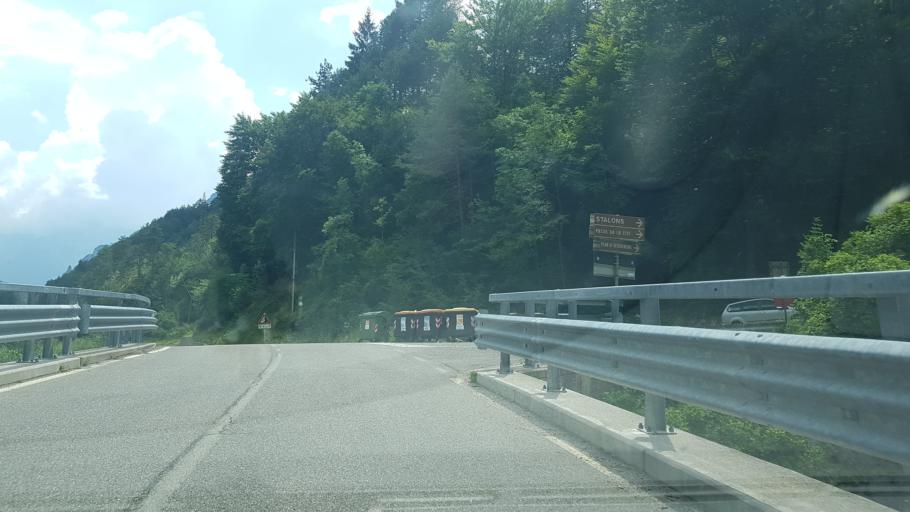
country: IT
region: Friuli Venezia Giulia
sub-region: Provincia di Udine
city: Moggio Udinese
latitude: 46.4788
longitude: 13.1894
